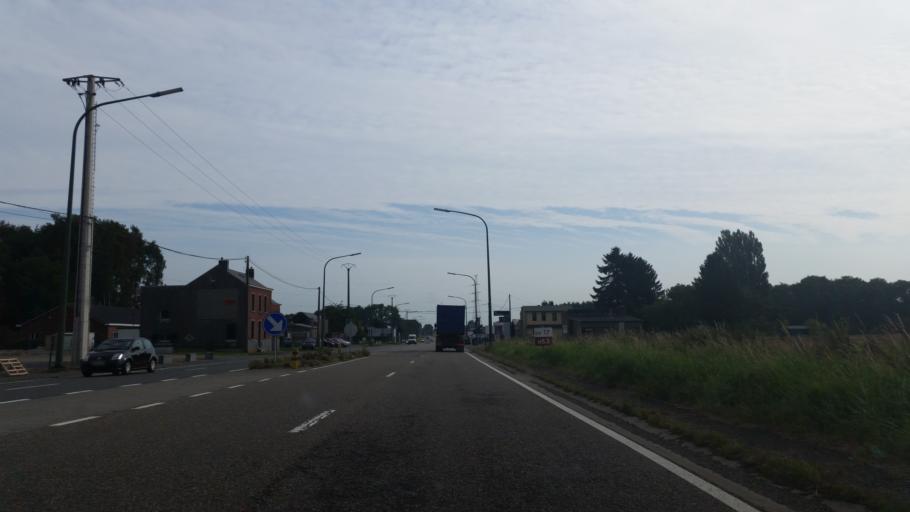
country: BE
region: Wallonia
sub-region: Province de Liege
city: Nandrin
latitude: 50.5195
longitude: 5.4153
